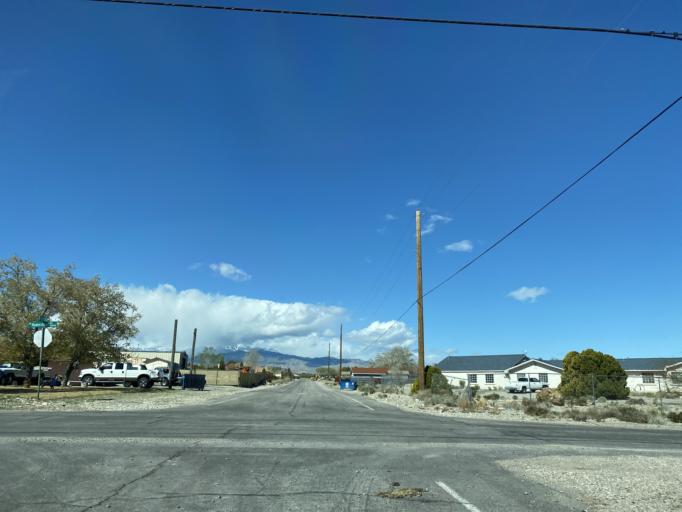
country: US
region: Nevada
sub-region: Clark County
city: North Las Vegas
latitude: 36.3302
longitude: -115.2828
